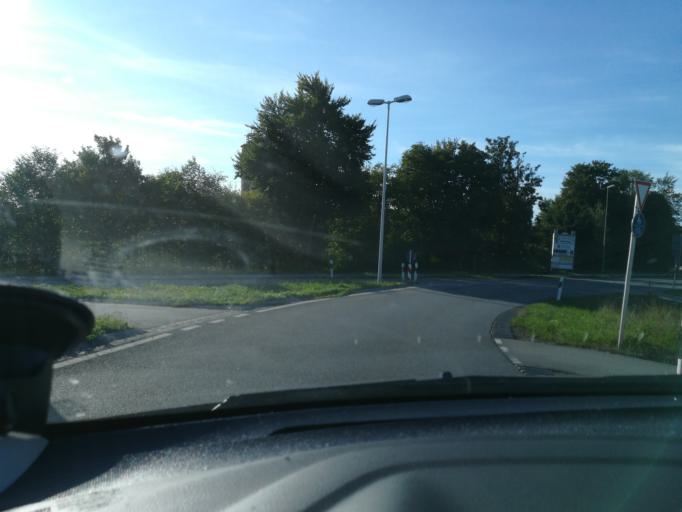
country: DE
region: Bavaria
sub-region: Upper Bavaria
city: Miesbach
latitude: 47.7945
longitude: 11.8406
